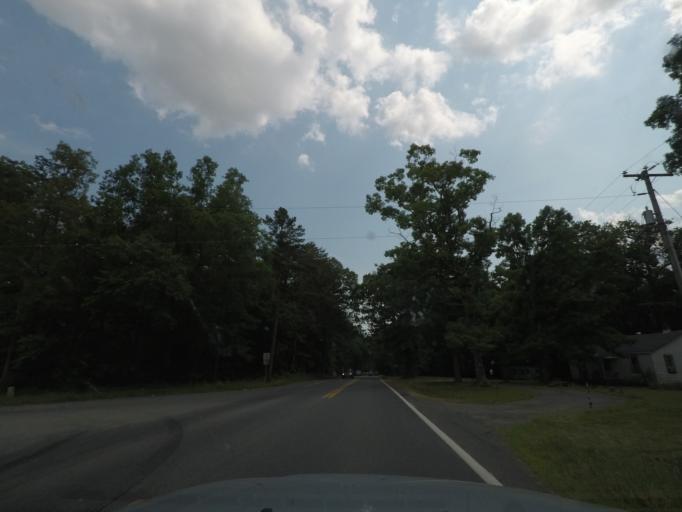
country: US
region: Virginia
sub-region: Orange County
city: Gordonsville
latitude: 38.0071
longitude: -78.1918
